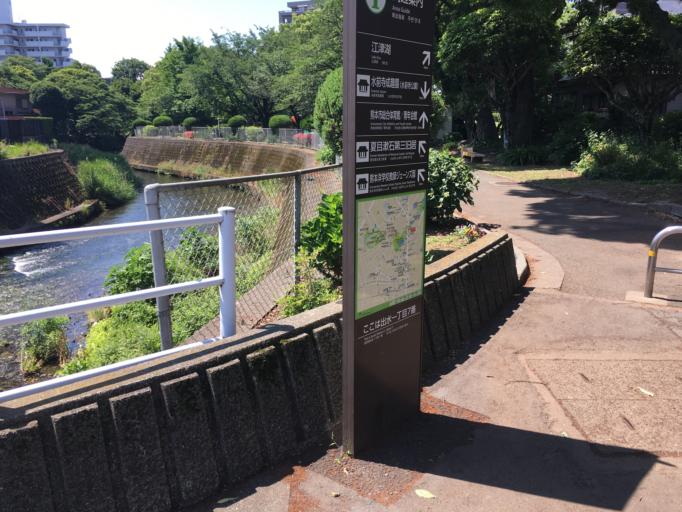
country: JP
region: Kumamoto
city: Kumamoto
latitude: 32.7885
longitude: 130.7343
